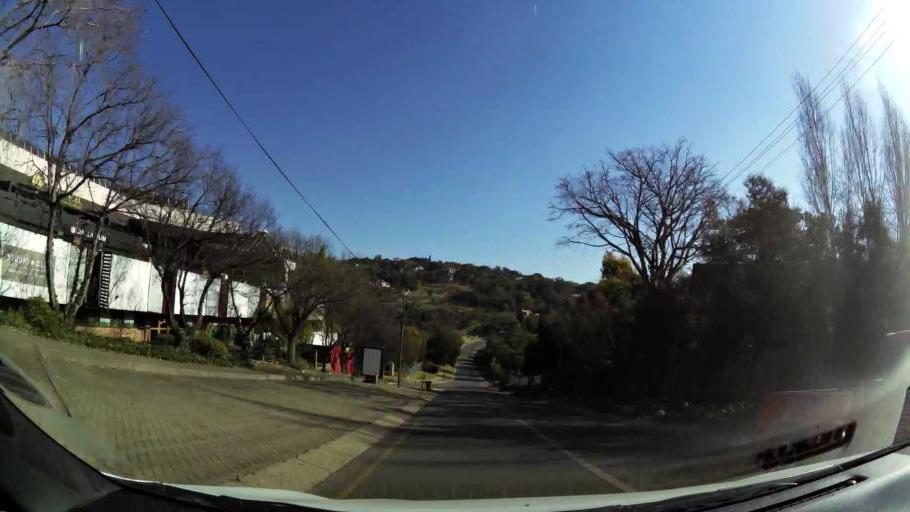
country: ZA
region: Gauteng
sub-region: City of Tshwane Metropolitan Municipality
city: Pretoria
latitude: -25.7912
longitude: 28.2533
